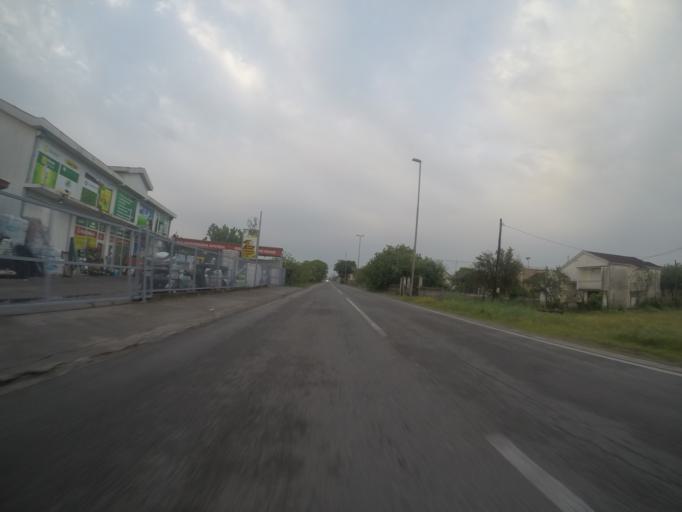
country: ME
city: Mojanovici
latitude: 42.3373
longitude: 19.2212
